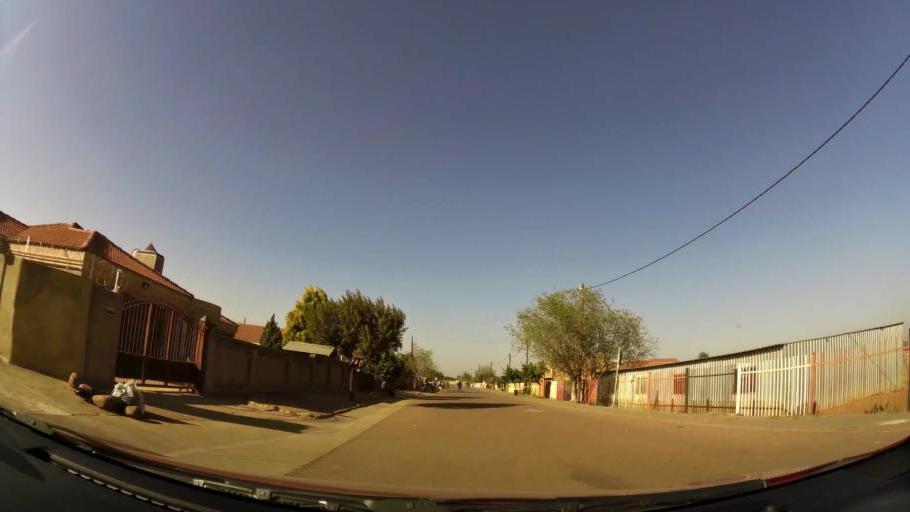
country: ZA
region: Gauteng
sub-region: City of Tshwane Metropolitan Municipality
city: Mabopane
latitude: -25.5880
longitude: 28.1077
